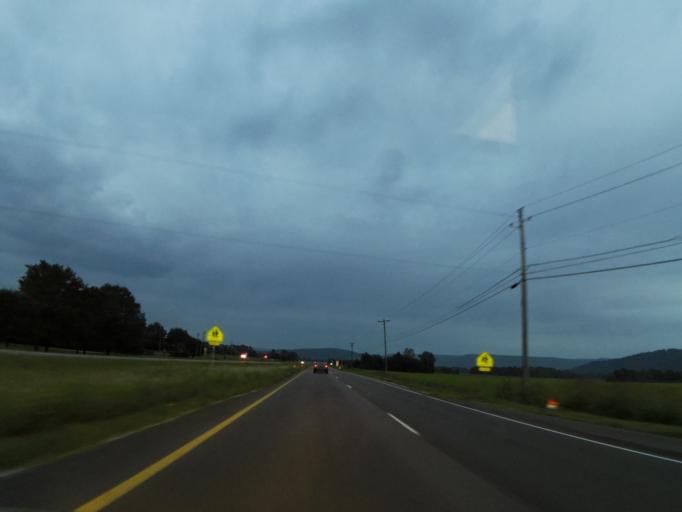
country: US
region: Alabama
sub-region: Madison County
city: Moores Mill
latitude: 34.7390
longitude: -86.4379
